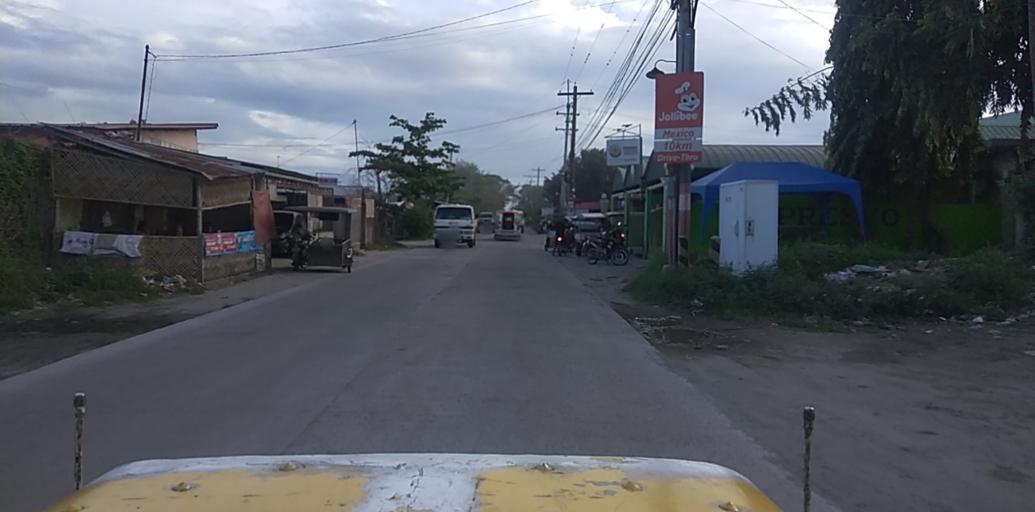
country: PH
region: Central Luzon
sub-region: Province of Pampanga
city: San Antonio
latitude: 15.1475
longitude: 120.6906
